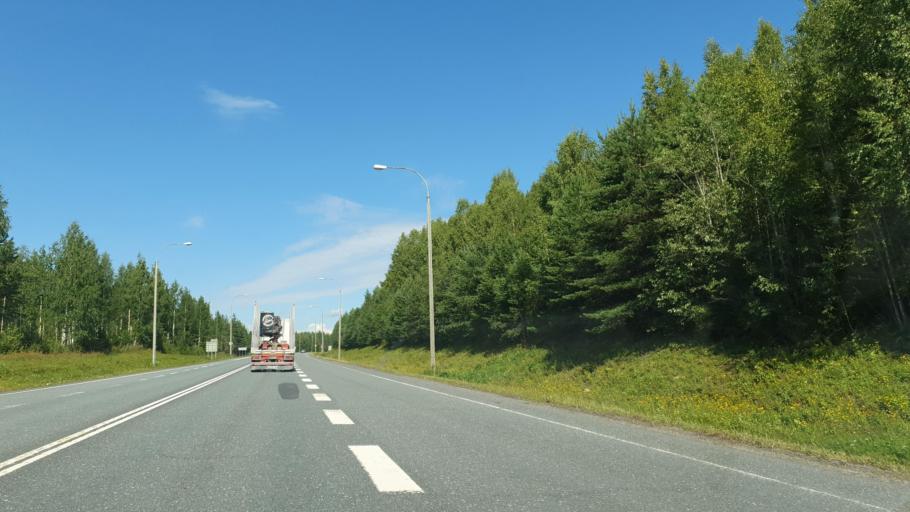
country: FI
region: Northern Savo
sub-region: Ylae-Savo
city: Iisalmi
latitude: 63.5947
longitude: 27.2202
